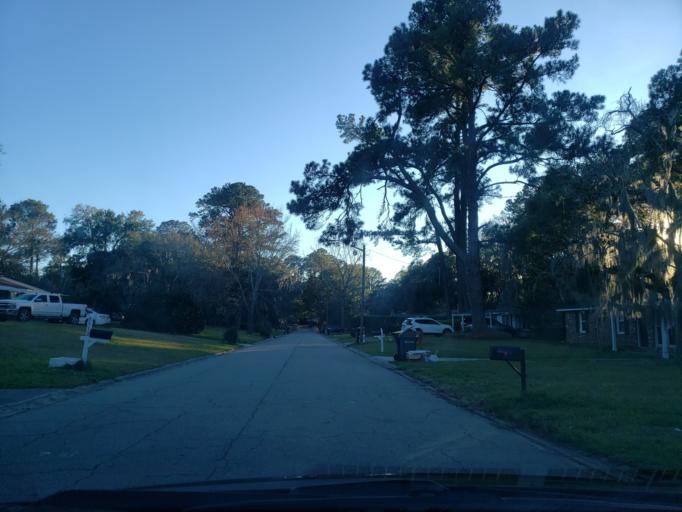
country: US
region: Georgia
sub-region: Chatham County
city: Isle of Hope
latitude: 31.9944
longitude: -81.1107
